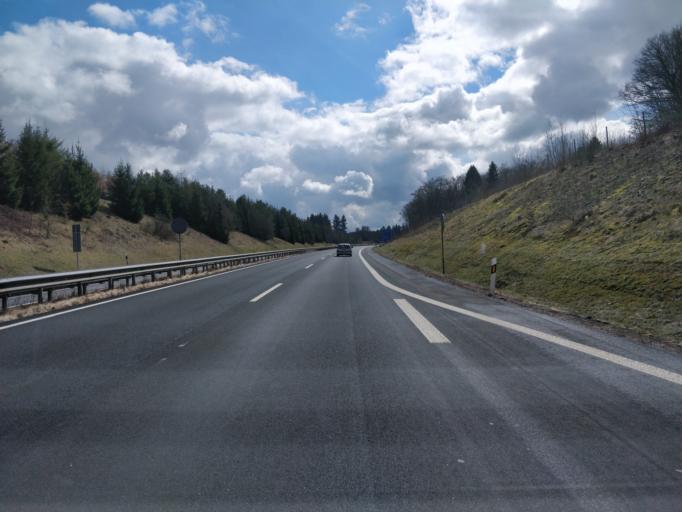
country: DE
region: Rheinland-Pfalz
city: Darscheid
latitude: 50.2054
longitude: 6.8850
